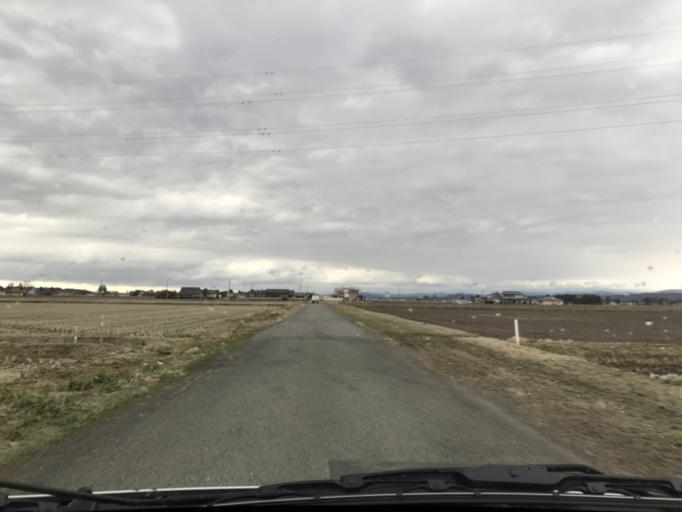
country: JP
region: Iwate
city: Mizusawa
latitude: 39.0785
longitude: 141.1563
